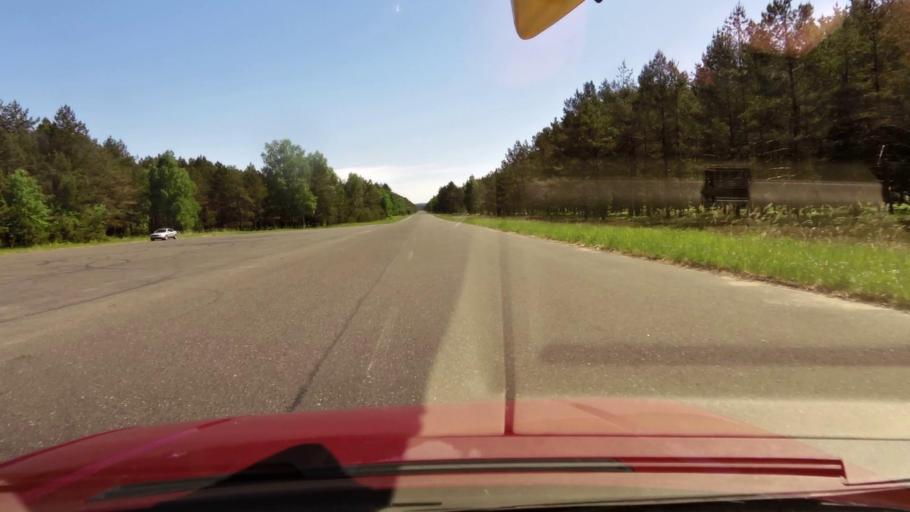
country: PL
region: West Pomeranian Voivodeship
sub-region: Powiat koszalinski
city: Bobolice
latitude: 54.0703
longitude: 16.5207
